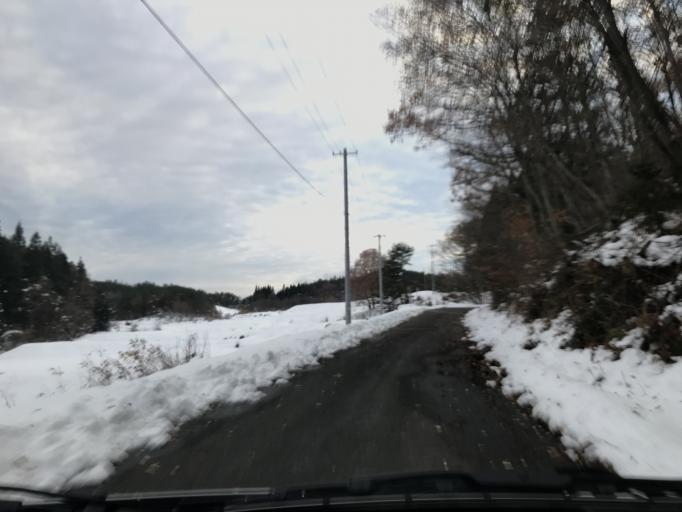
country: JP
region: Iwate
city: Mizusawa
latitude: 39.0393
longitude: 141.0186
